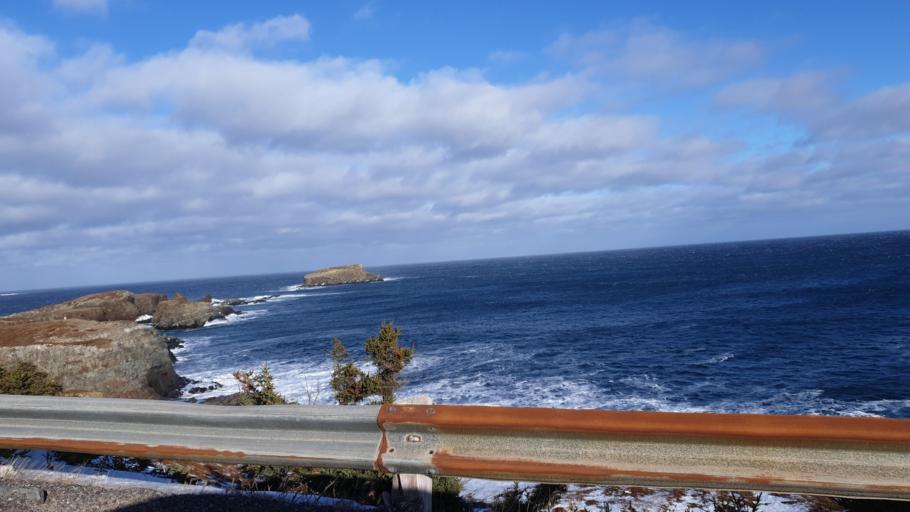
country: CA
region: Newfoundland and Labrador
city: Bonavista
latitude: 48.6243
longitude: -53.0183
